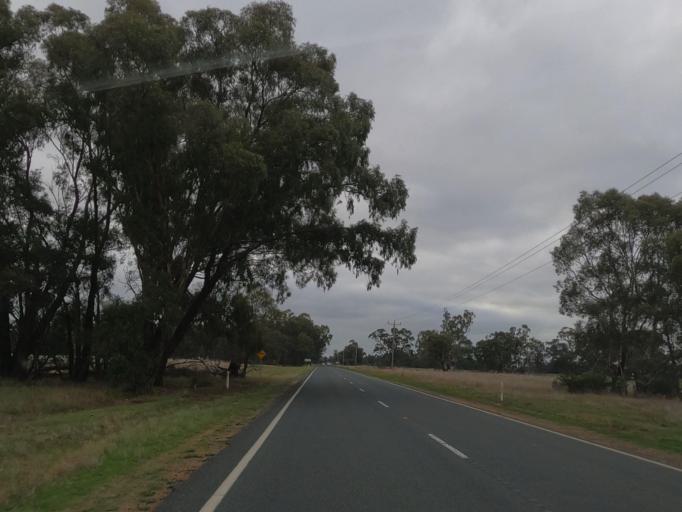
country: AU
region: Victoria
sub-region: Greater Bendigo
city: Long Gully
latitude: -36.4228
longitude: 143.9722
